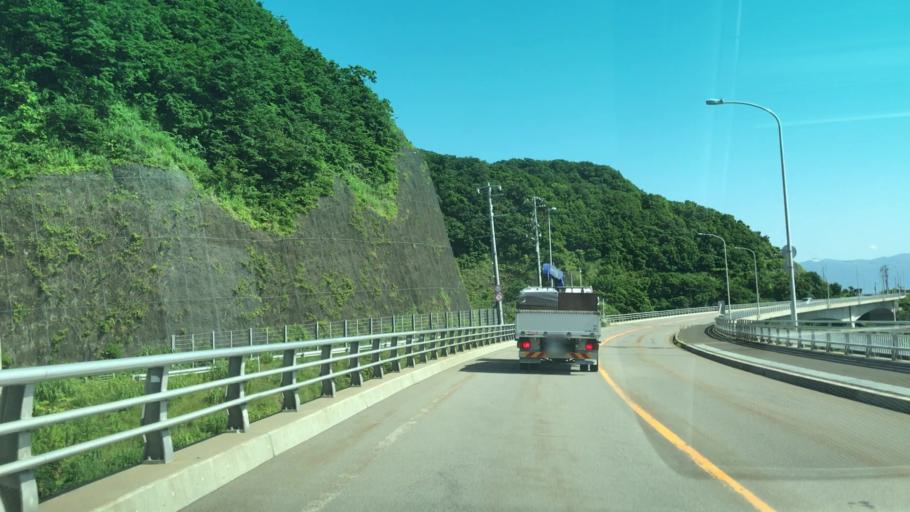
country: JP
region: Hokkaido
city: Iwanai
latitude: 43.1273
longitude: 140.4422
